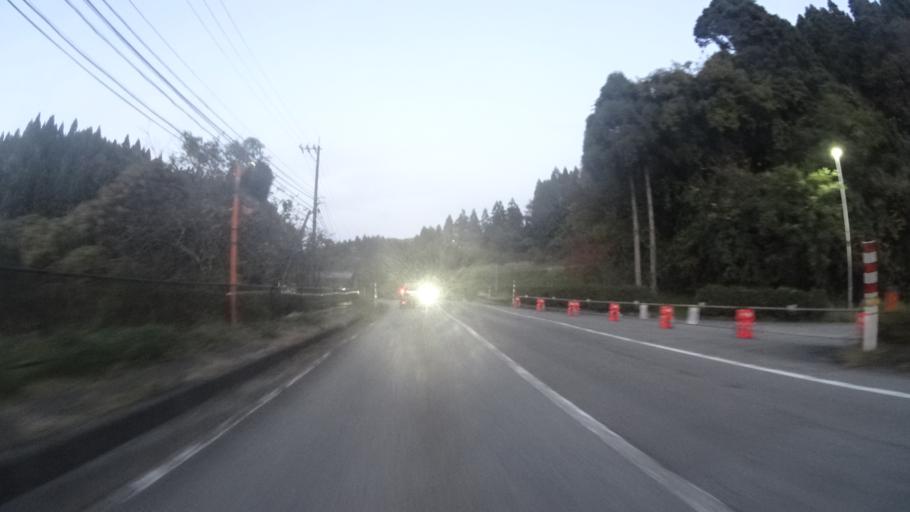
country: JP
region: Ishikawa
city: Nanao
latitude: 37.3491
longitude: 136.8618
